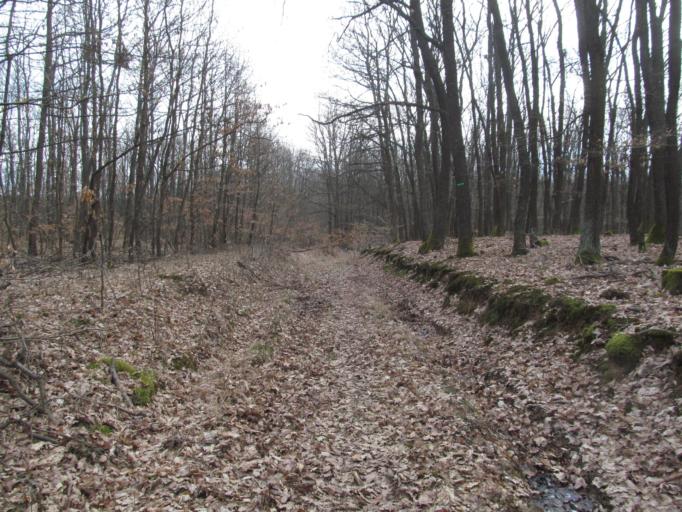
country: HU
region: Borsod-Abauj-Zemplen
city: Putnok
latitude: 48.4613
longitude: 20.4676
